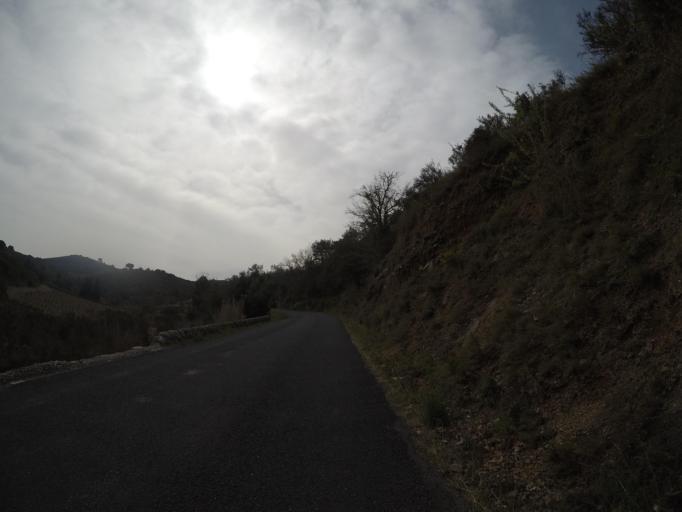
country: FR
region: Languedoc-Roussillon
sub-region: Departement des Pyrenees-Orientales
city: Estagel
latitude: 42.7499
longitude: 2.7225
